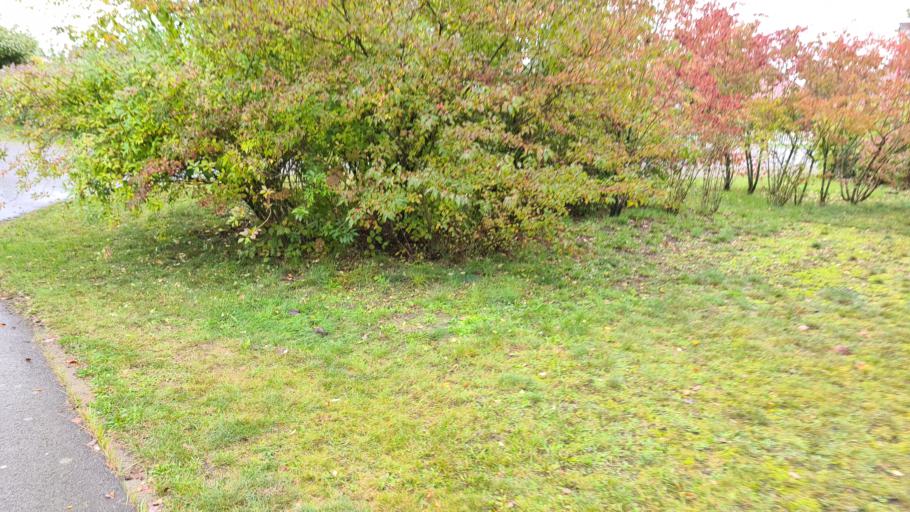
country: DE
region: Brandenburg
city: Altdobern
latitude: 51.6439
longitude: 14.0200
